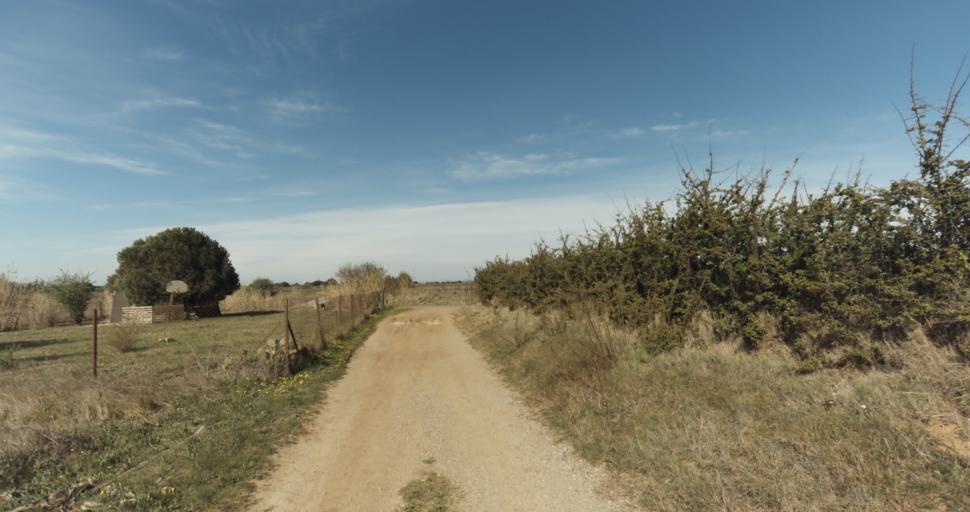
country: FR
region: Languedoc-Roussillon
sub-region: Departement de l'Herault
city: Marseillan
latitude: 43.3450
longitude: 3.5142
